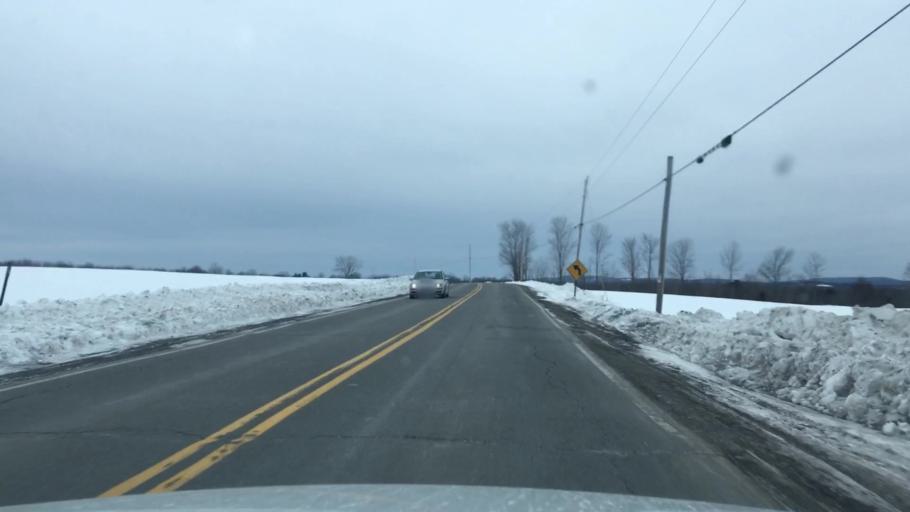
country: US
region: Maine
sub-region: Penobscot County
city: Corinna
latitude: 44.9455
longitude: -69.2132
